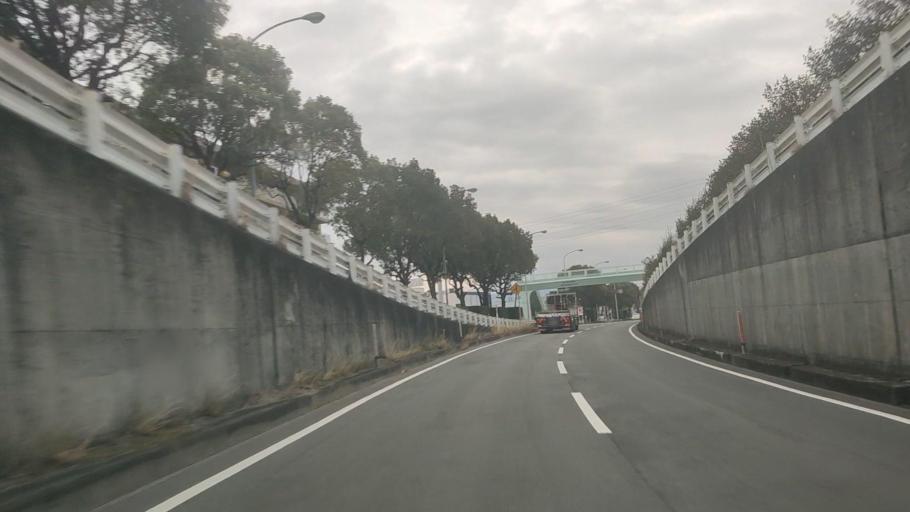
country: JP
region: Kumamoto
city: Ozu
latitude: 32.8544
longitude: 130.7843
